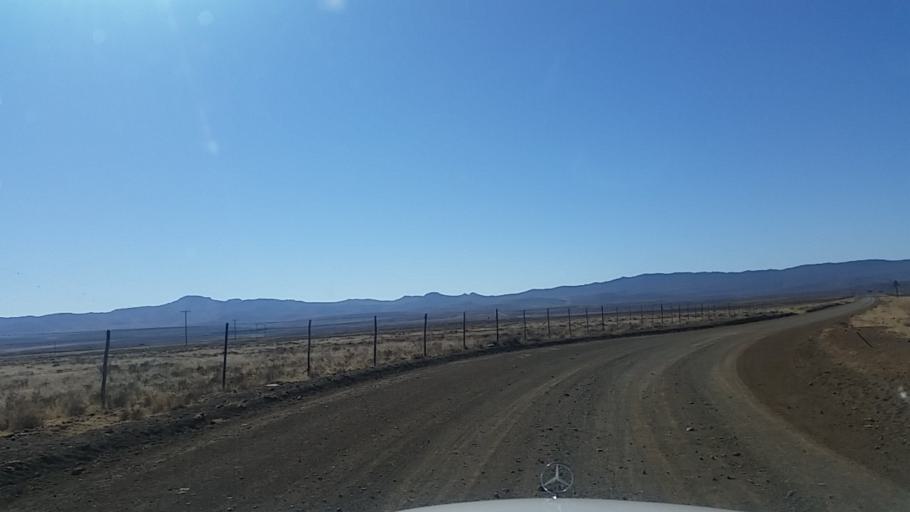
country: ZA
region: Eastern Cape
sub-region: Cacadu District Municipality
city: Graaff-Reinet
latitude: -31.9067
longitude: 24.7586
